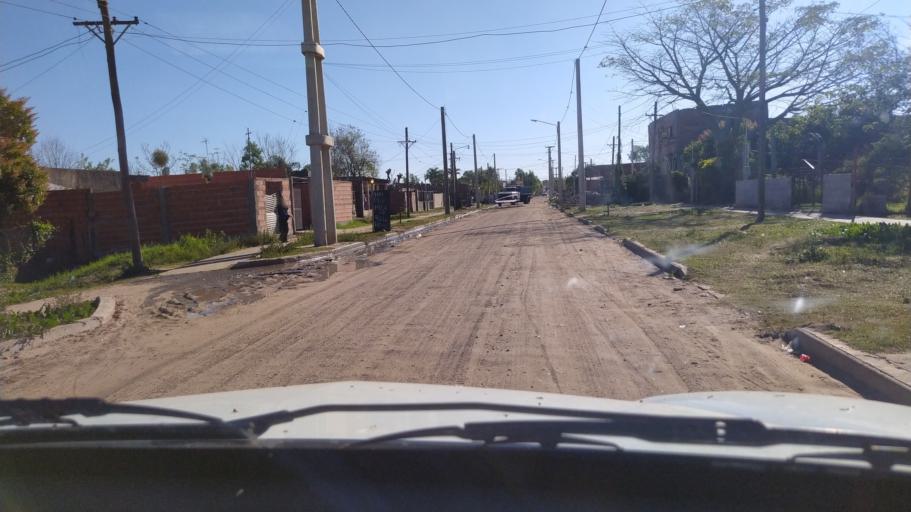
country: AR
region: Corrientes
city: Corrientes
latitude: -27.4974
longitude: -58.8065
